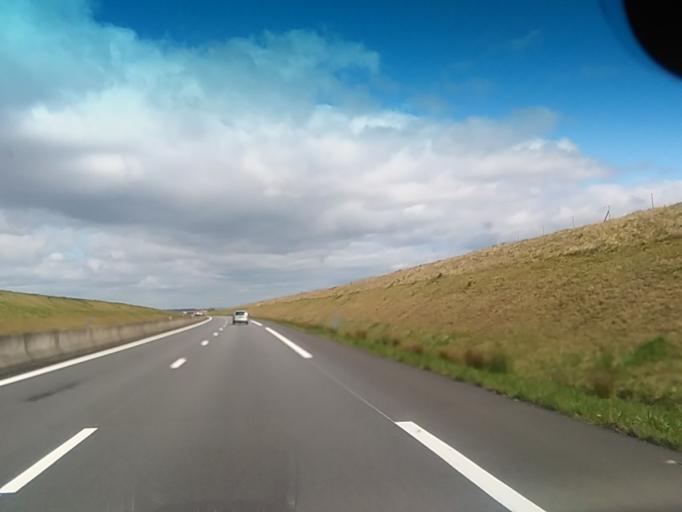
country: FR
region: Lower Normandy
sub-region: Departement du Calvados
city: Orbec
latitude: 49.0602
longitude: 0.4657
